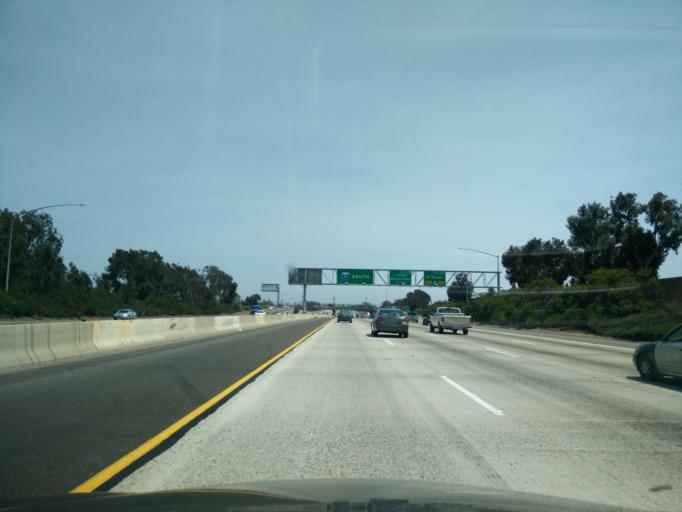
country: US
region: California
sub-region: San Diego County
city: Chula Vista
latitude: 32.6327
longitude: -117.0973
